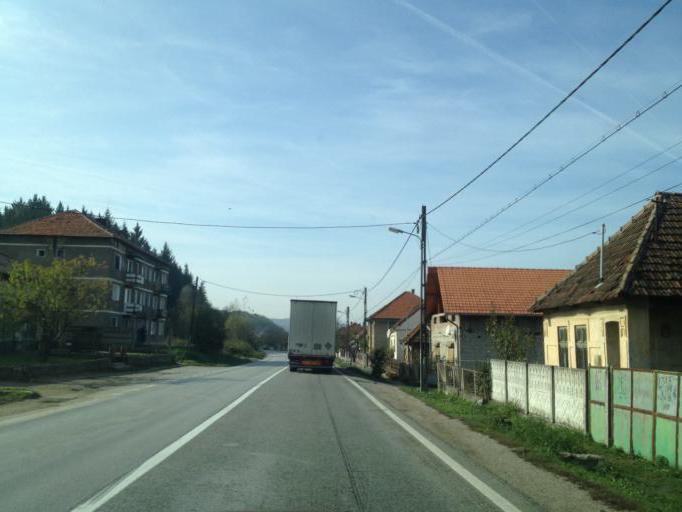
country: RO
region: Hunedoara
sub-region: Comuna Ilia
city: Ilia
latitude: 45.9152
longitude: 22.6156
